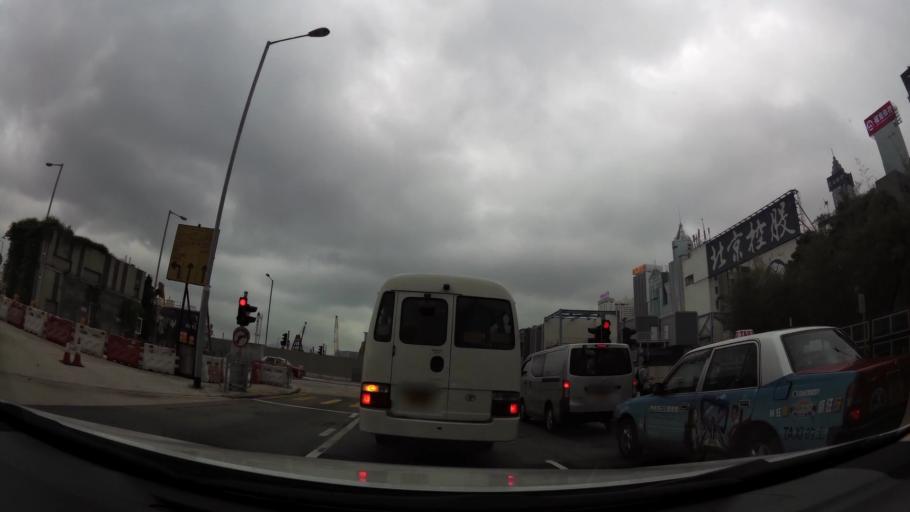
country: HK
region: Wanchai
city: Wan Chai
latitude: 22.2824
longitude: 114.1779
